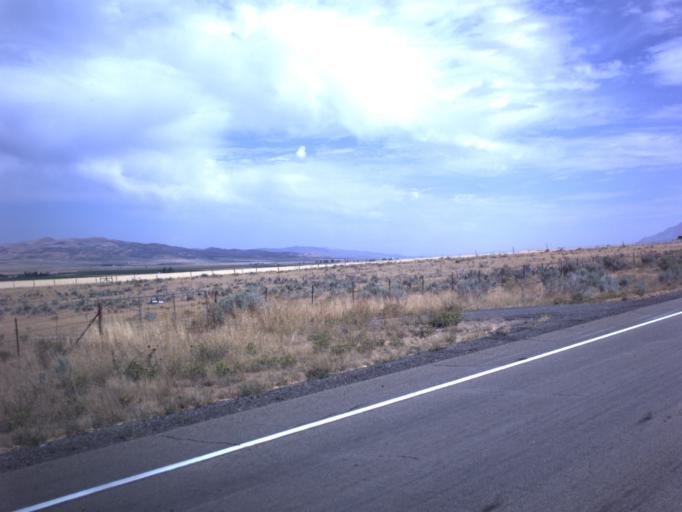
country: US
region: Utah
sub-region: Juab County
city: Nephi
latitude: 39.5036
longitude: -111.8739
